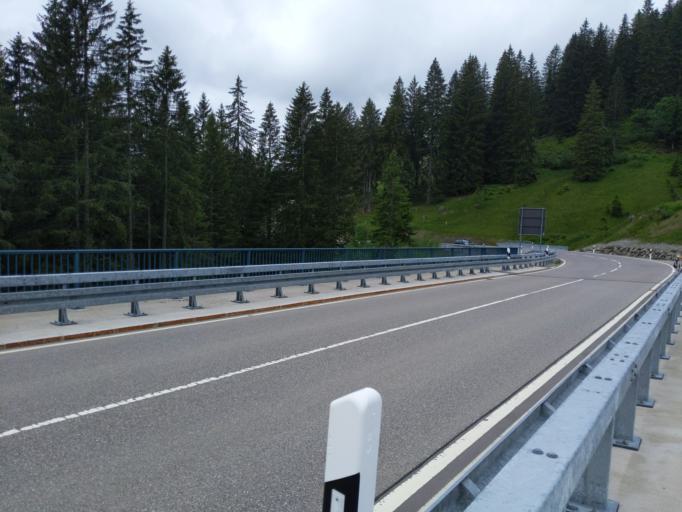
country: DE
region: Bavaria
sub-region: Swabia
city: Obermaiselstein
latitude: 47.4377
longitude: 10.1752
